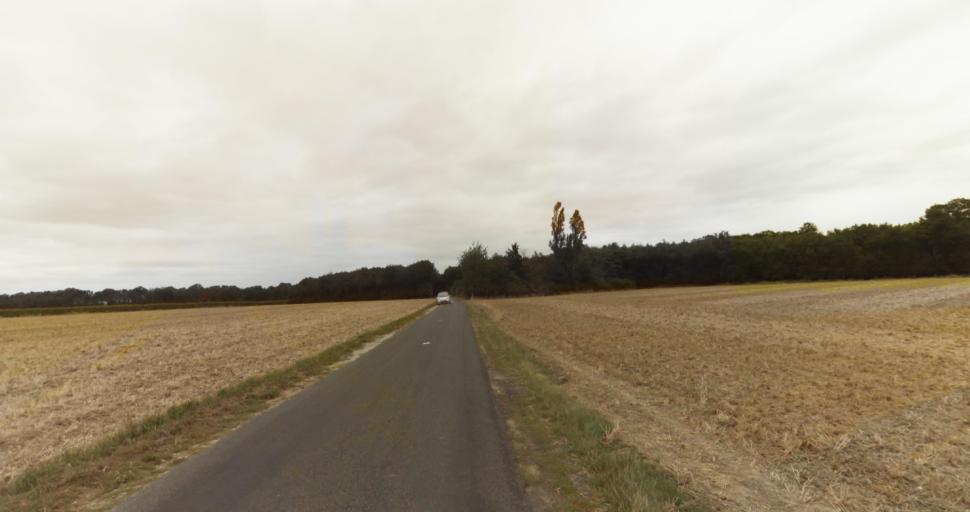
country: FR
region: Haute-Normandie
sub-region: Departement de l'Eure
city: Evreux
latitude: 48.9817
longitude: 1.2350
